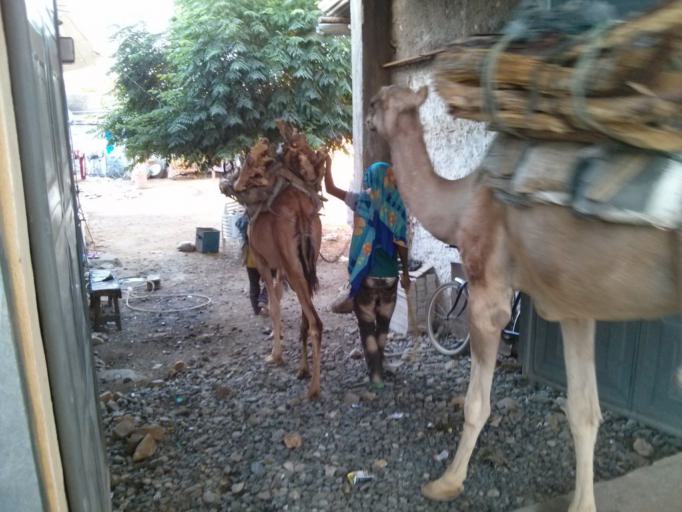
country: ET
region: Tigray
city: Aksum
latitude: 14.1244
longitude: 38.7325
